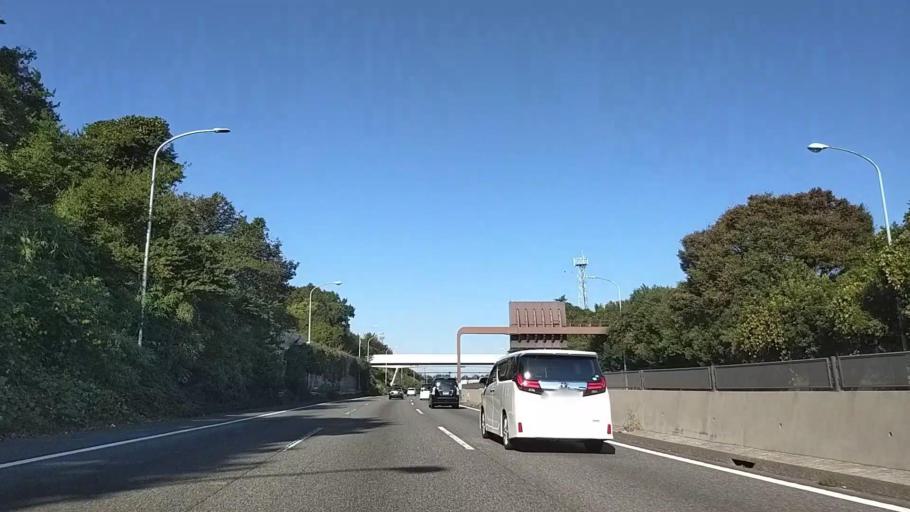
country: JP
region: Kanagawa
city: Yokohama
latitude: 35.4556
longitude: 139.5504
